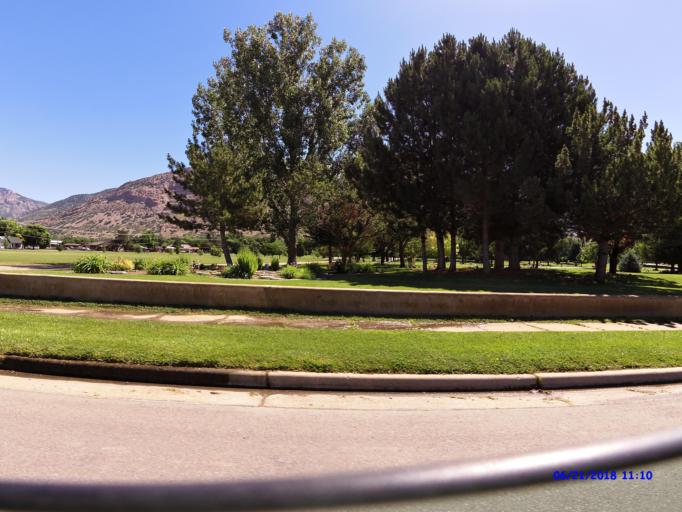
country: US
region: Utah
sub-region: Weber County
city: Harrisville
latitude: 41.2651
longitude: -111.9589
